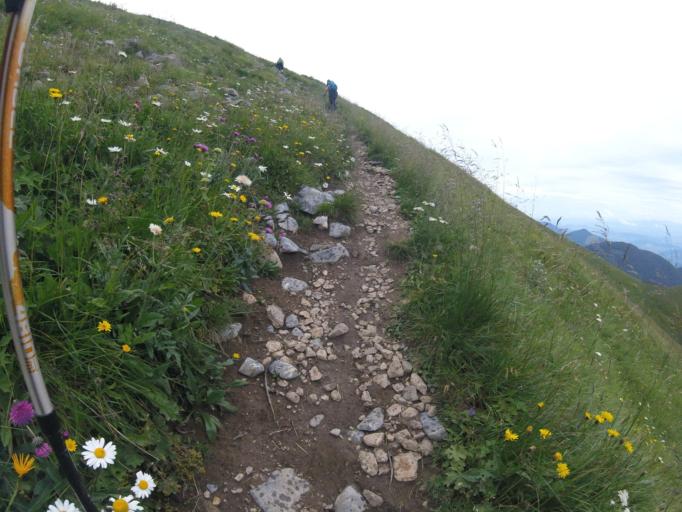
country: SK
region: Zilinsky
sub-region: Okres Zilina
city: Terchova
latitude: 49.1874
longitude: 19.0552
